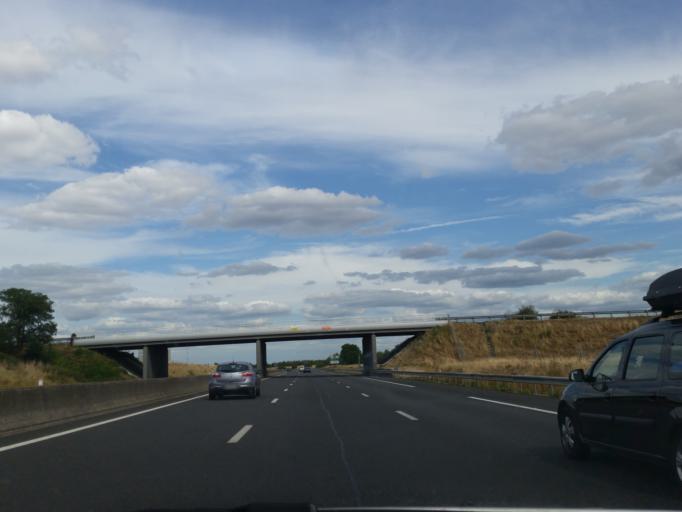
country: FR
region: Centre
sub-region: Departement du Loir-et-Cher
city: Villebarou
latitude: 47.6177
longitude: 1.3256
